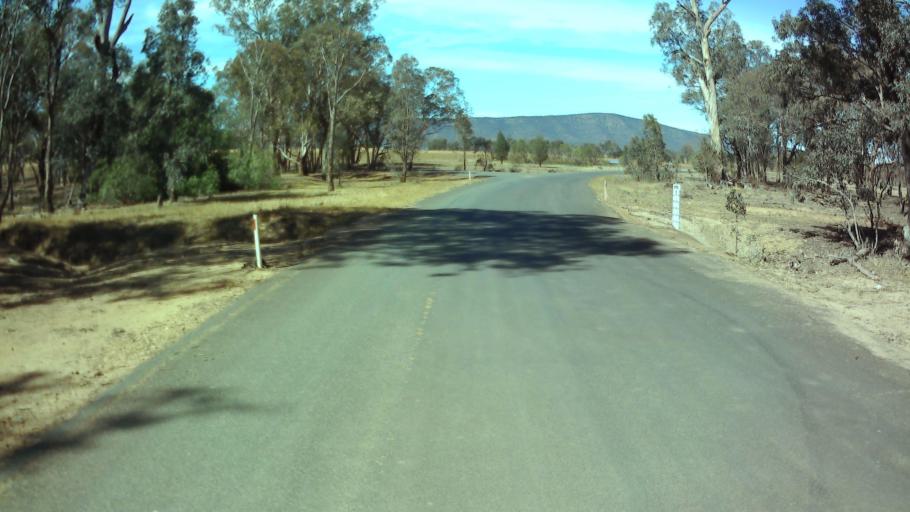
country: AU
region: New South Wales
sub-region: Weddin
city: Grenfell
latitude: -33.9399
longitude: 148.0788
